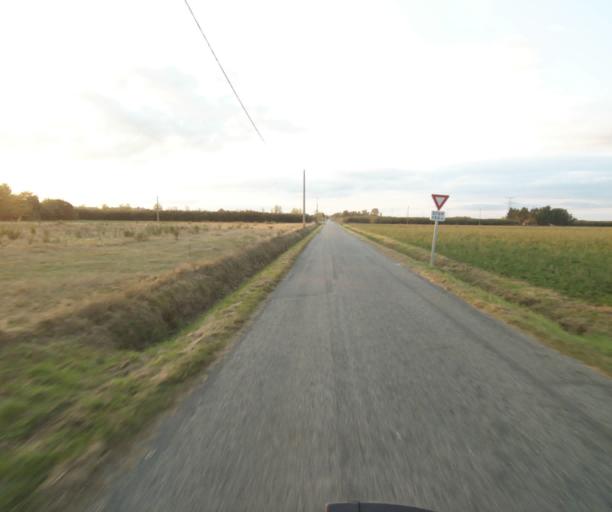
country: FR
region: Midi-Pyrenees
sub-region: Departement du Tarn-et-Garonne
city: Verdun-sur-Garonne
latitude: 43.8301
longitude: 1.2280
